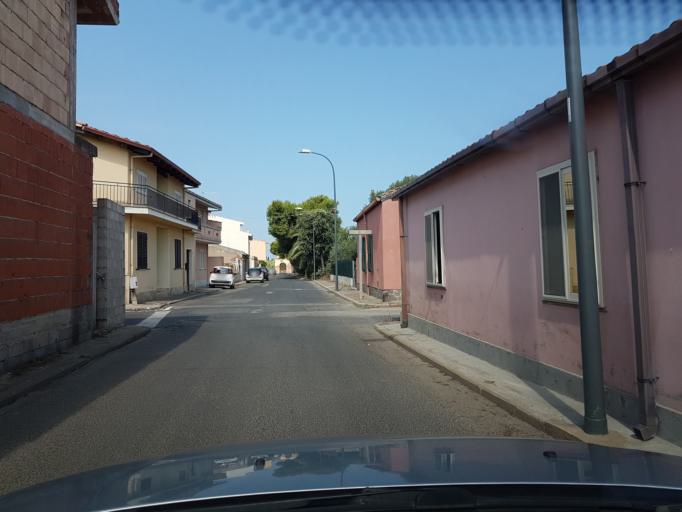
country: IT
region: Sardinia
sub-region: Provincia di Oristano
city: Donigala Fenugheddu
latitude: 39.9377
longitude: 8.5735
